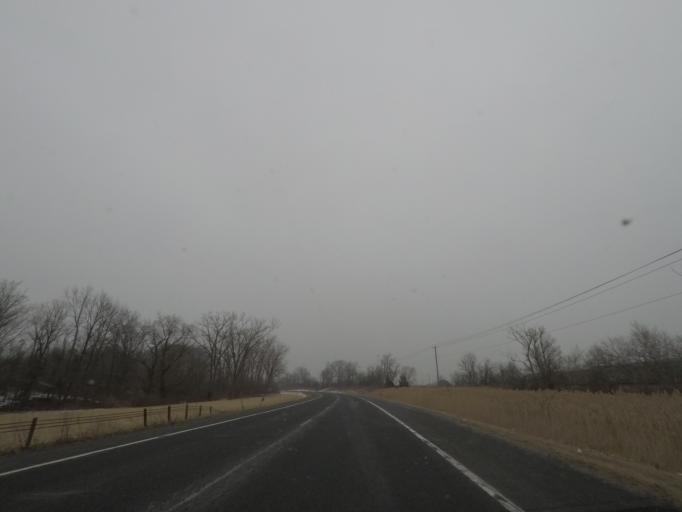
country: US
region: New York
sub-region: Albany County
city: Delmar
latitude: 42.5687
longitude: -73.8528
